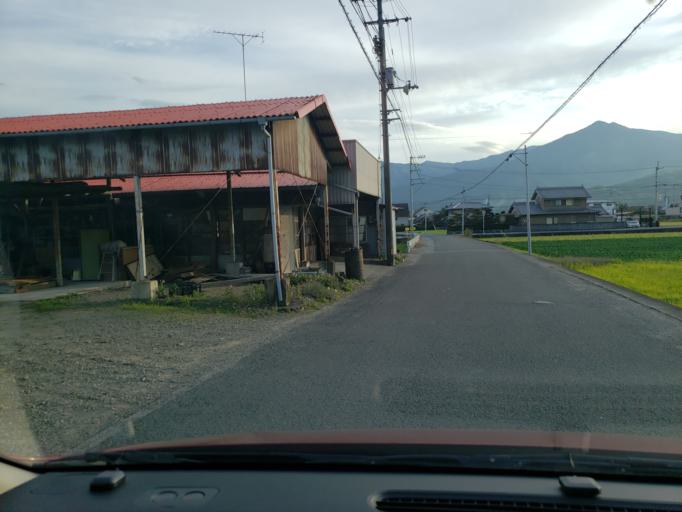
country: JP
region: Tokushima
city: Wakimachi
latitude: 34.0765
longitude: 134.2279
